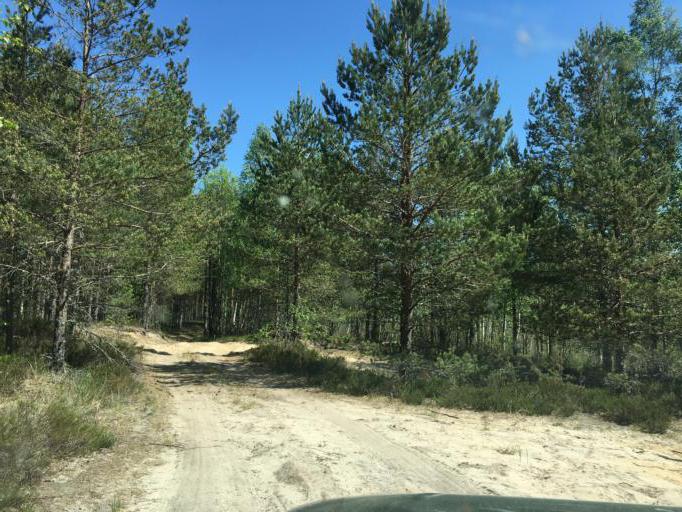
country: LV
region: Dundaga
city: Dundaga
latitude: 57.5684
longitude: 22.0073
